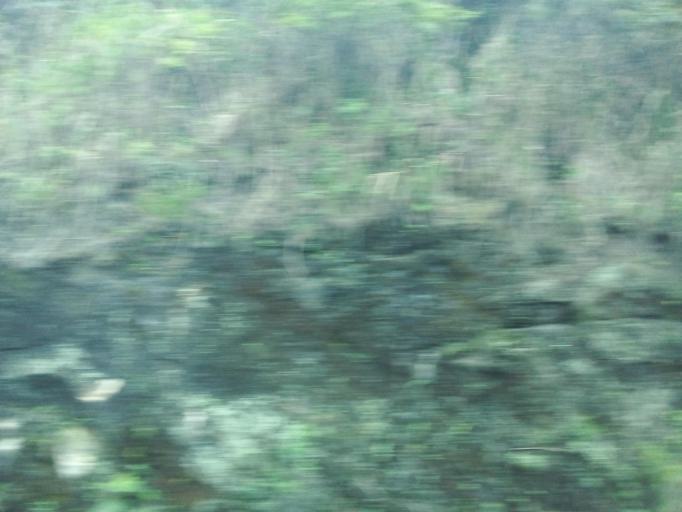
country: BR
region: Minas Gerais
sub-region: Joao Monlevade
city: Joao Monlevade
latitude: -19.8255
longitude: -43.1248
